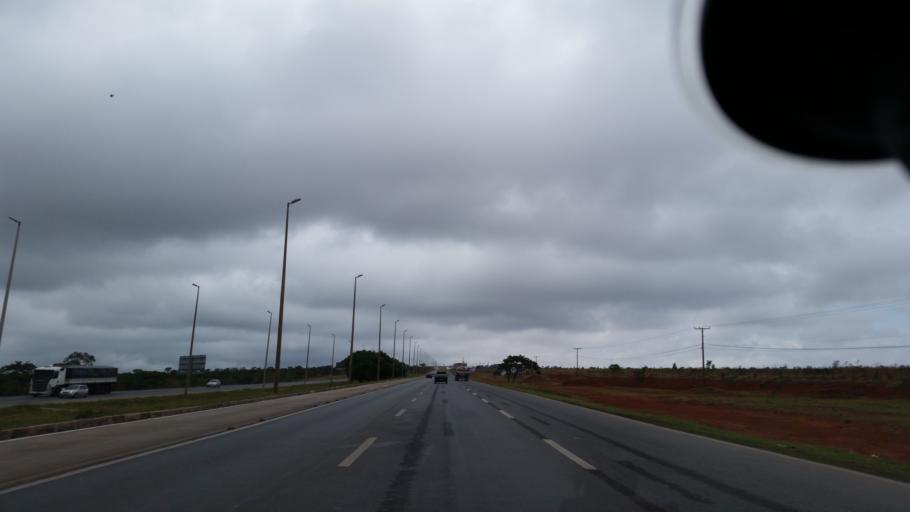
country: BR
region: Federal District
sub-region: Brasilia
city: Brasilia
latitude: -15.9568
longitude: -47.9941
